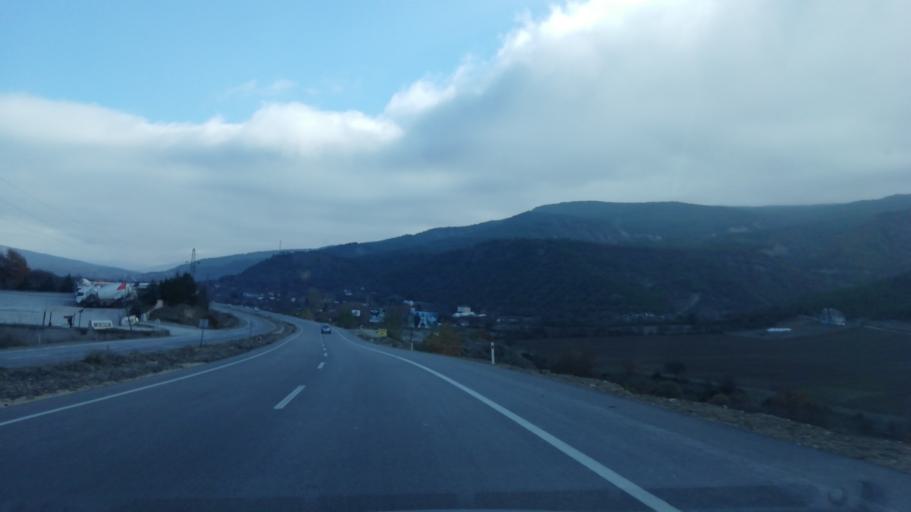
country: TR
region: Karabuk
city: Safranbolu
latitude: 41.2180
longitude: 32.7289
